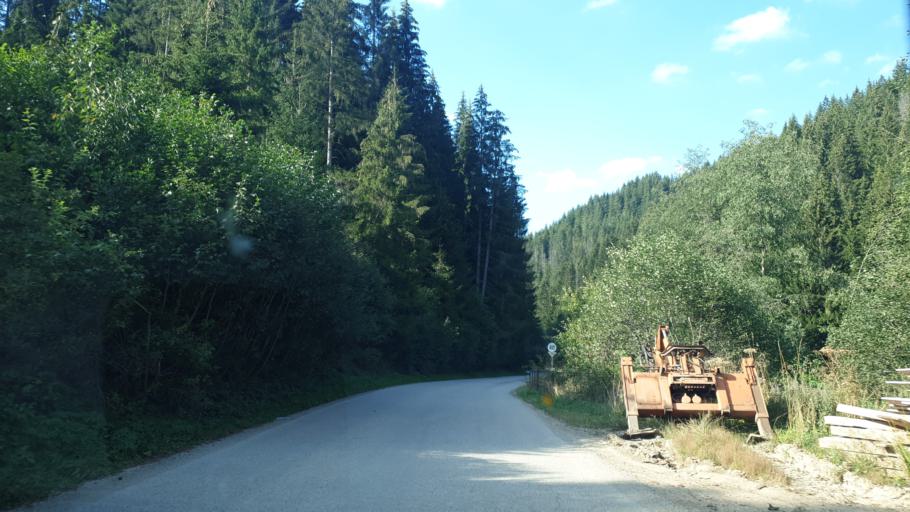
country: RS
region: Central Serbia
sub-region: Zlatiborski Okrug
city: Nova Varos
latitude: 43.4526
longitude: 19.8428
